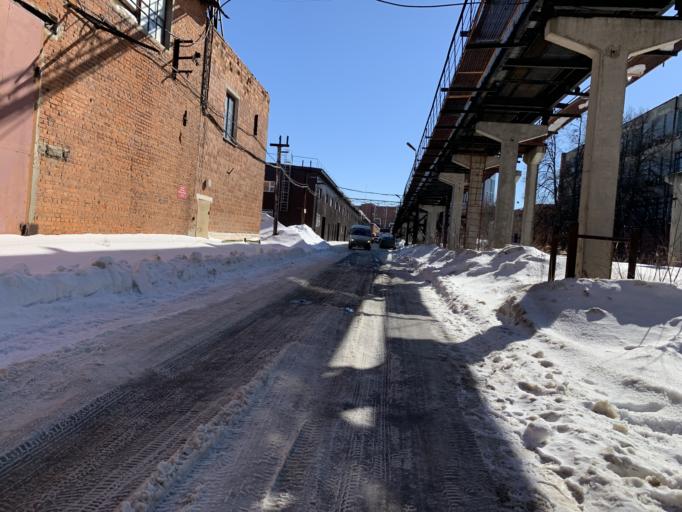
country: RU
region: Chuvashia
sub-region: Cheboksarskiy Rayon
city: Cheboksary
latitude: 56.1420
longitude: 47.2783
